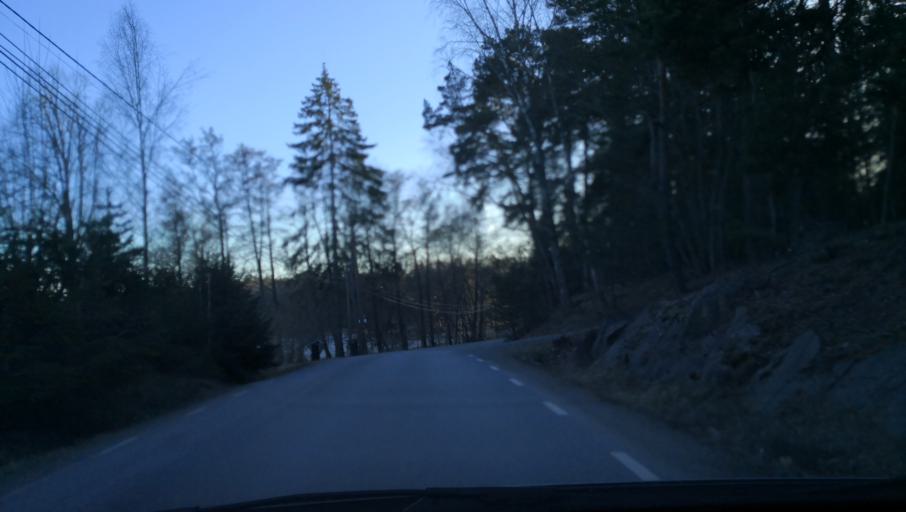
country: SE
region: Stockholm
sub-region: Varmdo Kommun
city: Gustavsberg
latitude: 59.3281
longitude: 18.4196
